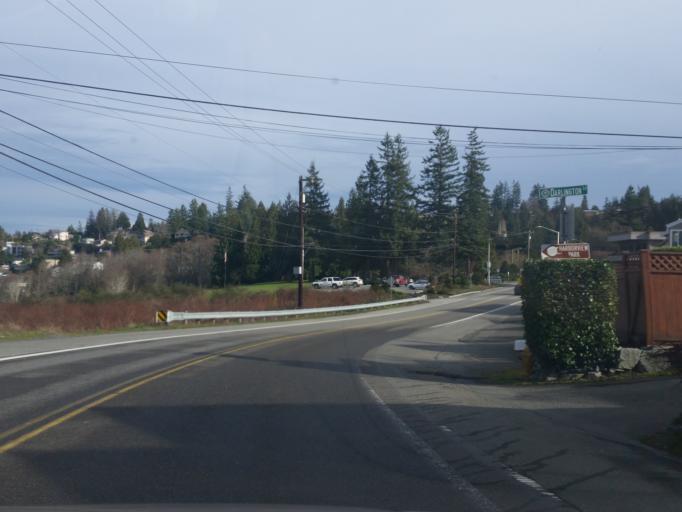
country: US
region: Washington
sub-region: Snohomish County
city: Mukilteo
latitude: 47.9572
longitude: -122.2541
